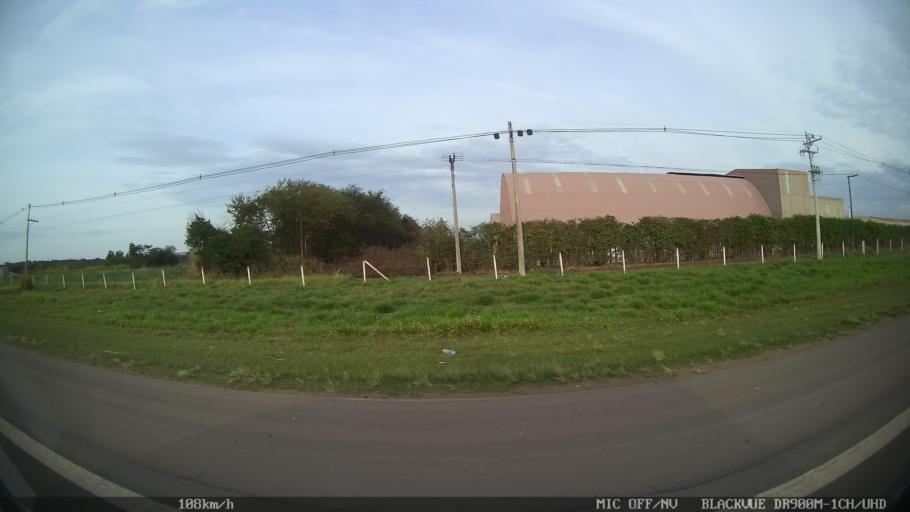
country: BR
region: Sao Paulo
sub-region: Iracemapolis
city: Iracemapolis
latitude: -22.6111
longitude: -47.4779
